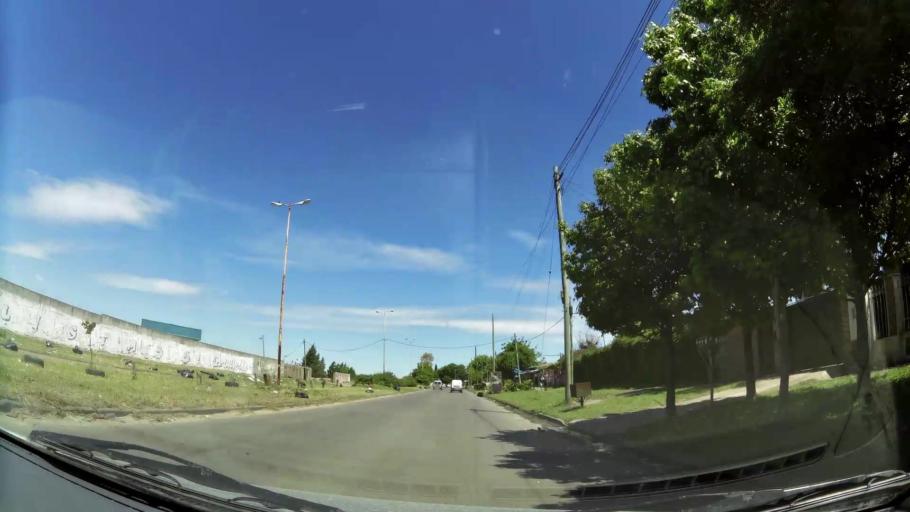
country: AR
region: Buenos Aires
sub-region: Partido de Lanus
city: Lanus
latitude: -34.7414
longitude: -58.3435
